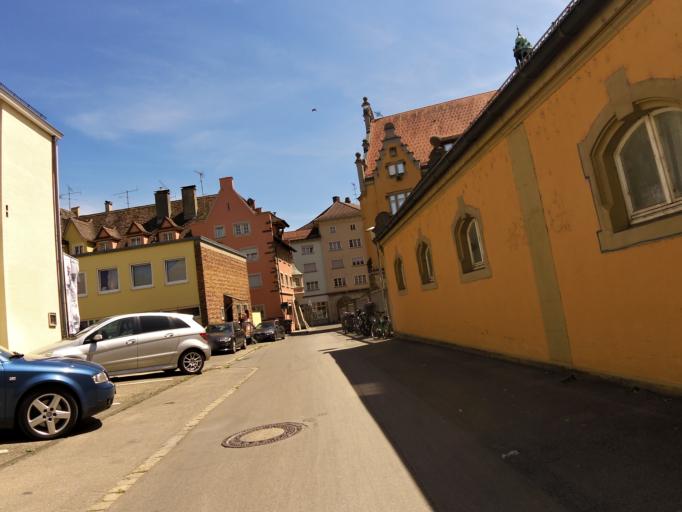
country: DE
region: Bavaria
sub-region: Swabia
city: Lindau
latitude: 47.5462
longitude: 9.6811
